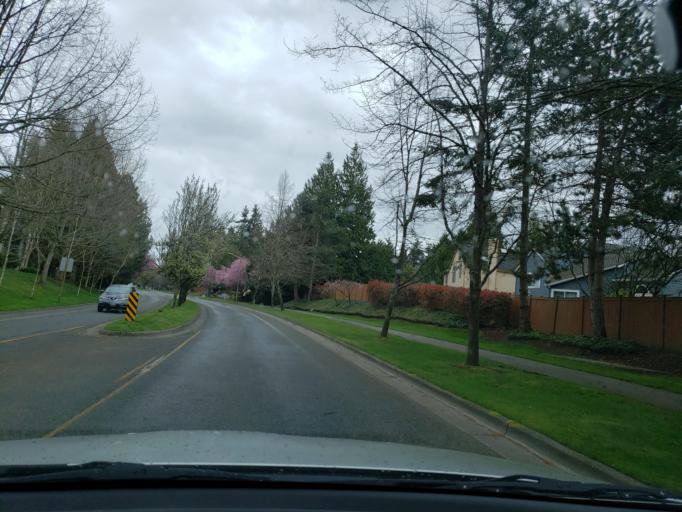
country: US
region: Washington
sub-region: Snohomish County
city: Meadowdale
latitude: 47.8860
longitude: -122.3063
